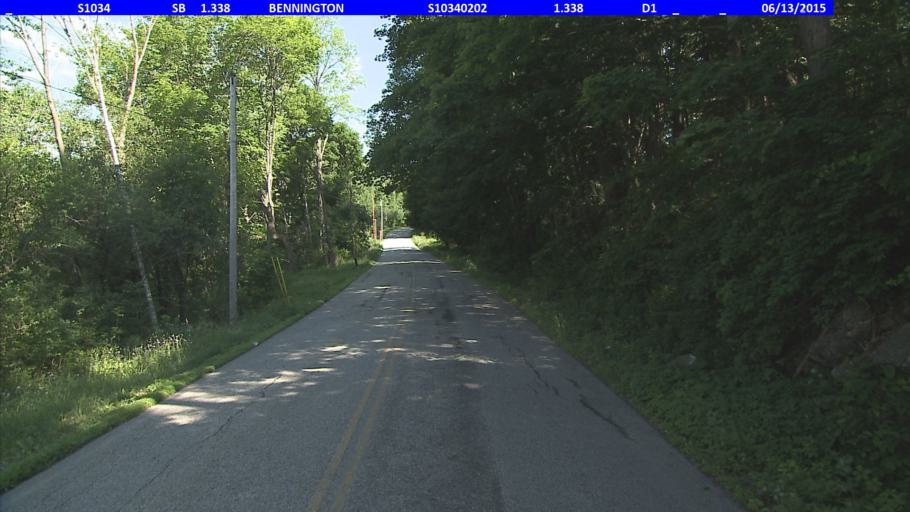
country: US
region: Vermont
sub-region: Bennington County
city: Bennington
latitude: 42.8701
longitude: -73.2107
